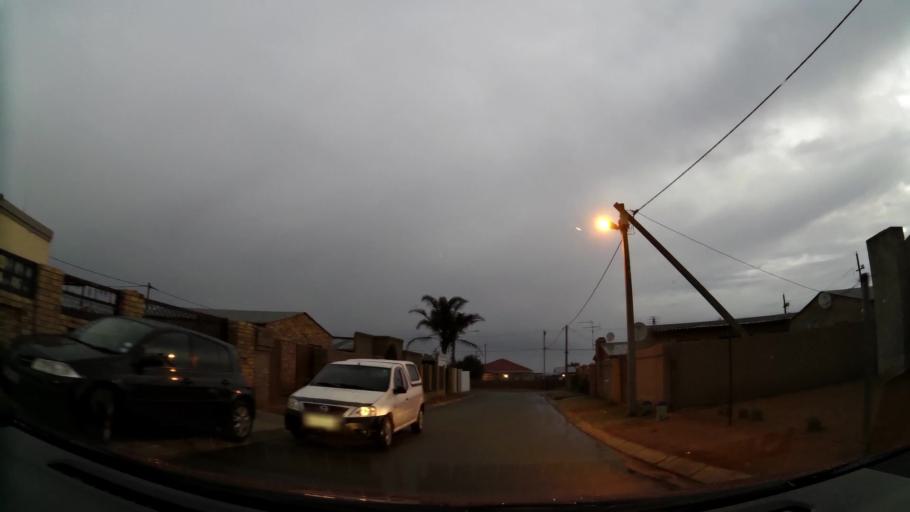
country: ZA
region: Gauteng
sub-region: West Rand District Municipality
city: Randfontein
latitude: -26.1777
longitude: 27.7859
